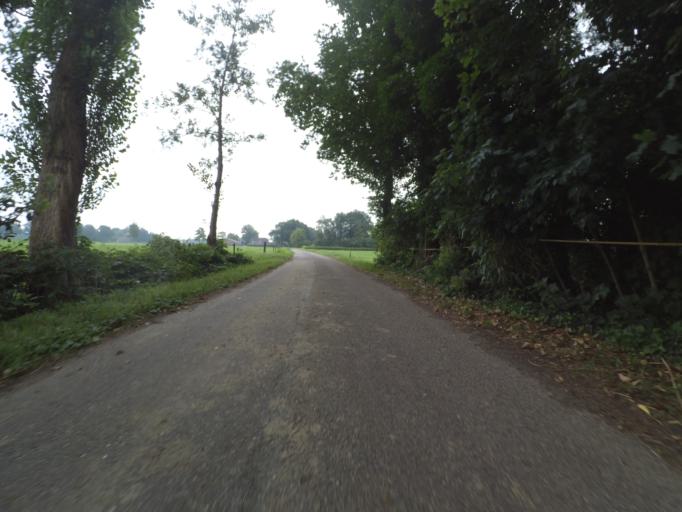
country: NL
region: Gelderland
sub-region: Gemeente Barneveld
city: Kootwijkerbroek
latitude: 52.1230
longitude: 5.6779
